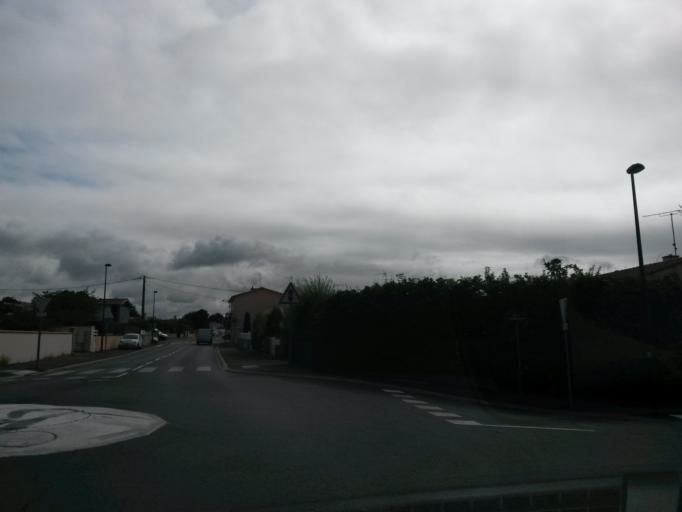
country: FR
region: Pays de la Loire
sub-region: Departement de la Vendee
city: Olonne-sur-Mer
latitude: 46.5242
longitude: -1.7763
